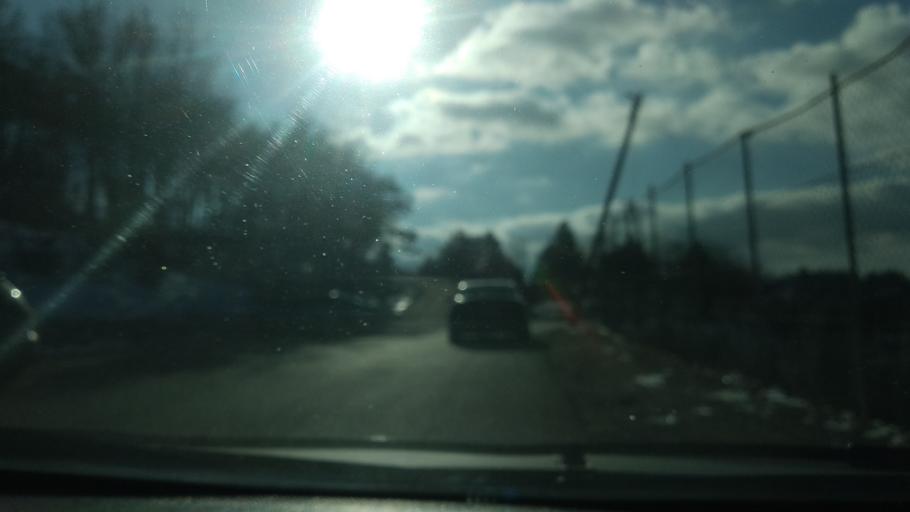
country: XK
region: Pristina
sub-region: Komuna e Prishtines
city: Pristina
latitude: 42.7124
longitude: 21.1688
